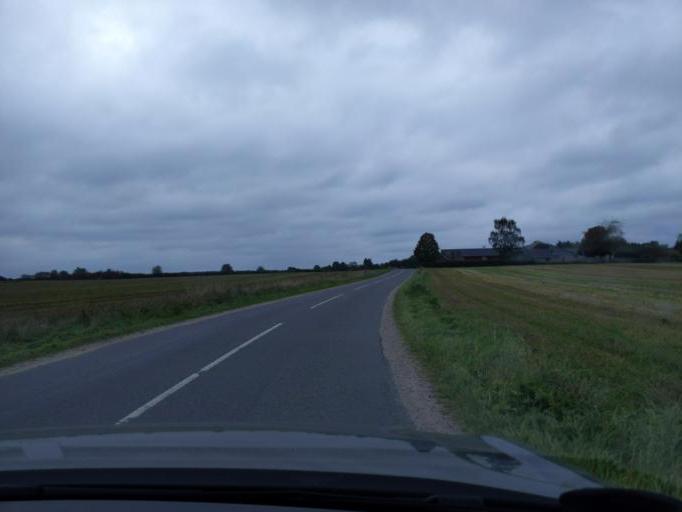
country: DK
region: Central Jutland
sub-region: Viborg Kommune
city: Bjerringbro
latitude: 56.5474
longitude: 9.6424
